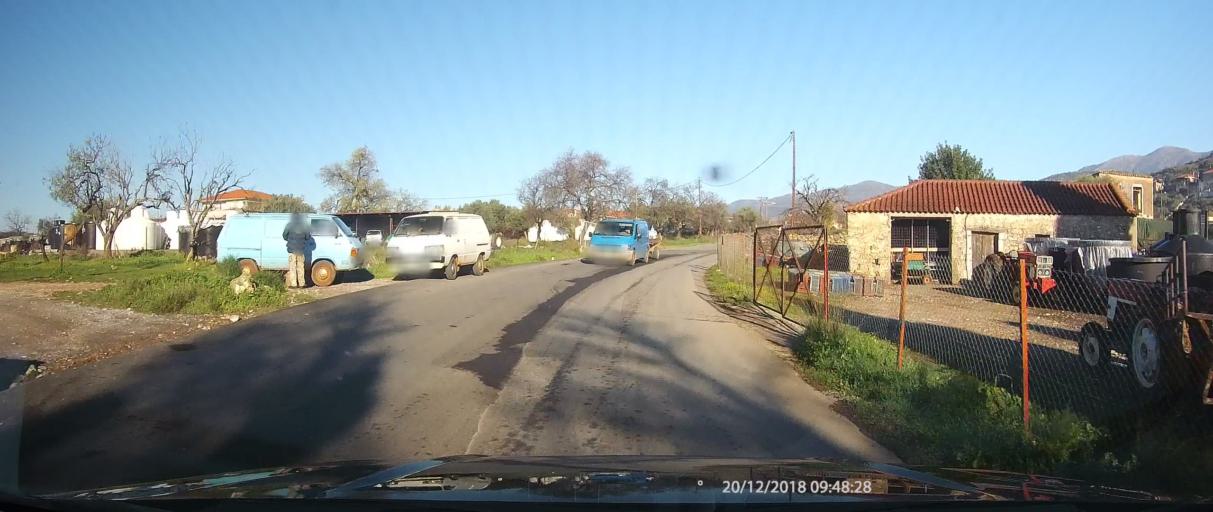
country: GR
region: Peloponnese
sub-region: Nomos Lakonias
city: Yerakion
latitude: 36.9908
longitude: 22.7017
